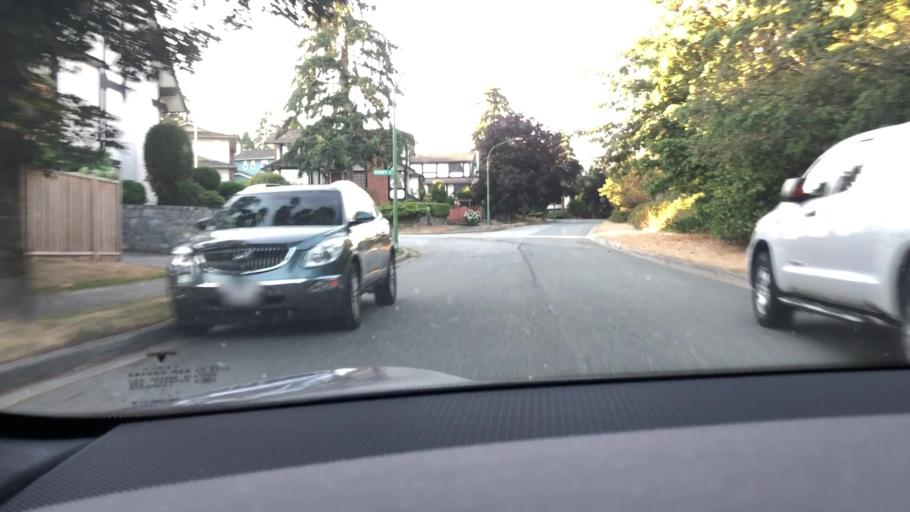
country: CA
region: British Columbia
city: New Westminster
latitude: 49.2085
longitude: -122.9715
